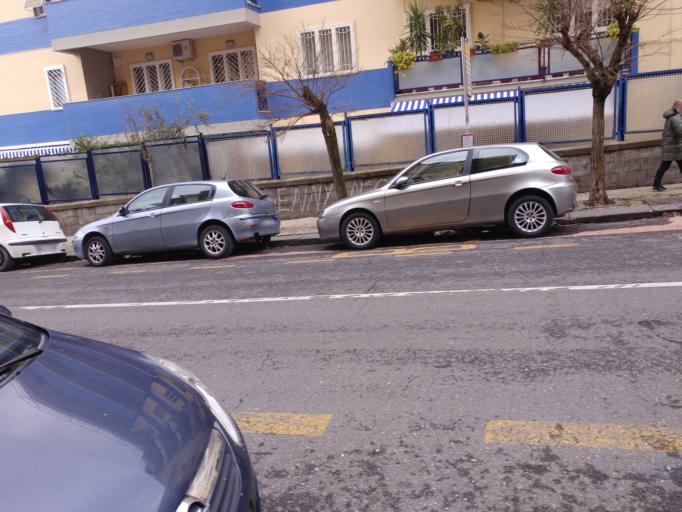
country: IT
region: Campania
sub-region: Provincia di Napoli
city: Napoli
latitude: 40.8574
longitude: 14.2285
